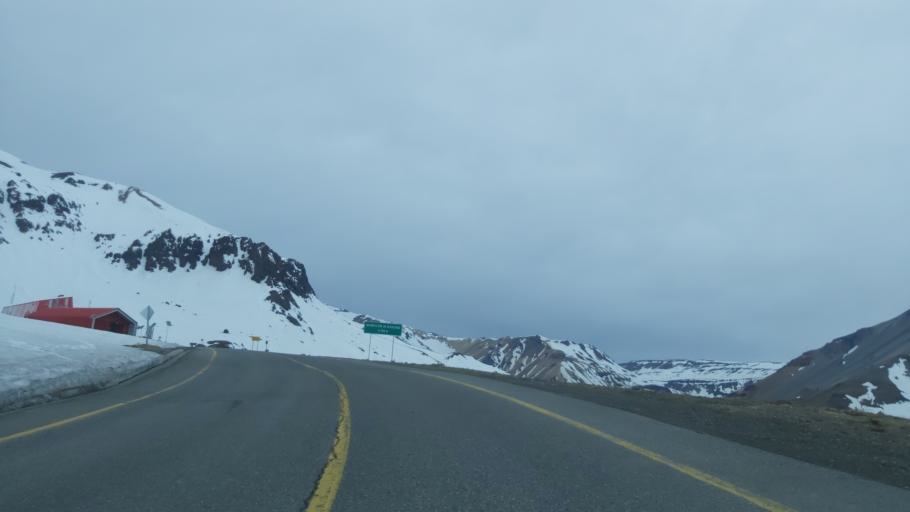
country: CL
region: Maule
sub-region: Provincia de Linares
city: Colbun
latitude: -36.0125
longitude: -70.4846
